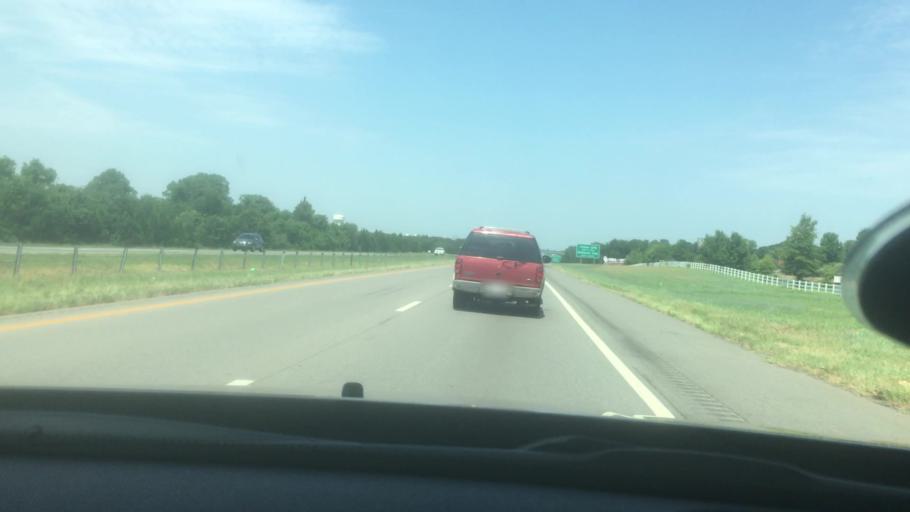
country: US
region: Oklahoma
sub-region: Oklahoma County
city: Midwest City
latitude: 35.4259
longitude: -97.3531
